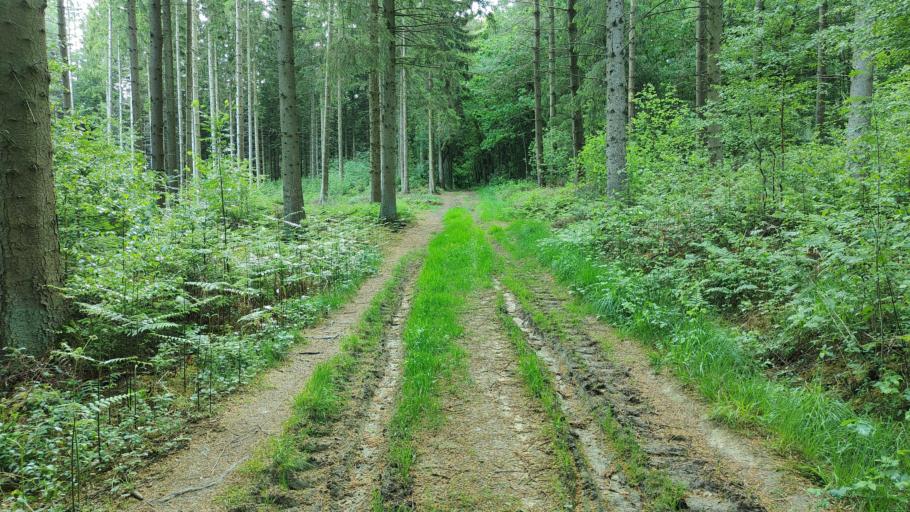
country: BE
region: Wallonia
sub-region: Province de Liege
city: La Calamine
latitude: 50.7072
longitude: 6.0520
